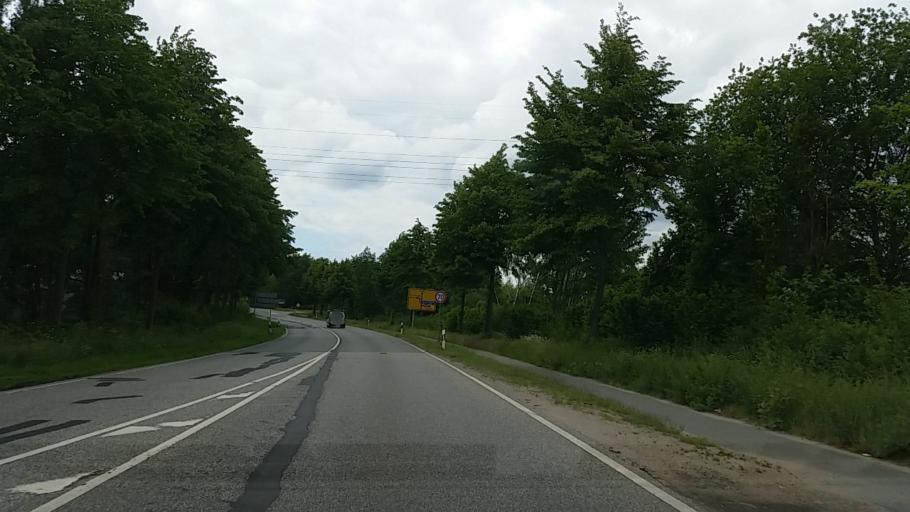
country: DE
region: Schleswig-Holstein
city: Reinbek
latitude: 53.5311
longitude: 10.2366
